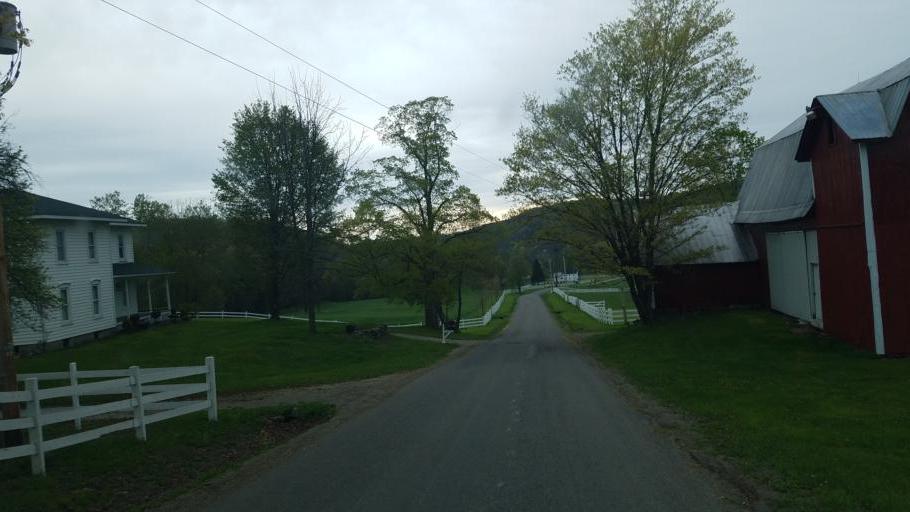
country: US
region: Pennsylvania
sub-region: Tioga County
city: Westfield
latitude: 42.0493
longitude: -77.4699
